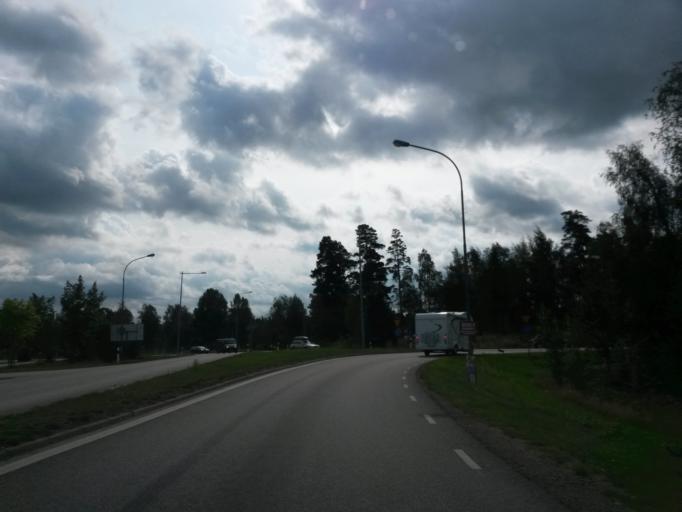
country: SE
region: Kronoberg
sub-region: Vaxjo Kommun
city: Vaexjoe
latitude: 56.9038
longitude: 14.8260
